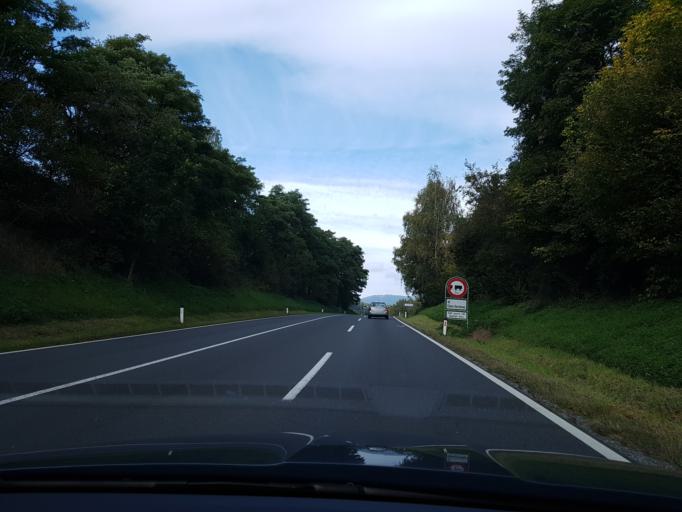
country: AT
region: Carinthia
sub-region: Politischer Bezirk Feldkirchen
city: Feldkirchen in Karnten
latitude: 46.7328
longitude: 14.0745
